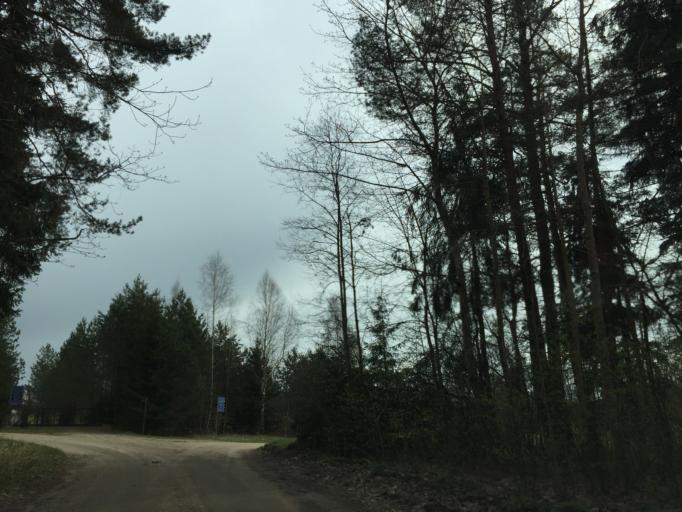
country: LV
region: Cesu Rajons
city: Cesis
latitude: 57.2932
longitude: 25.3147
